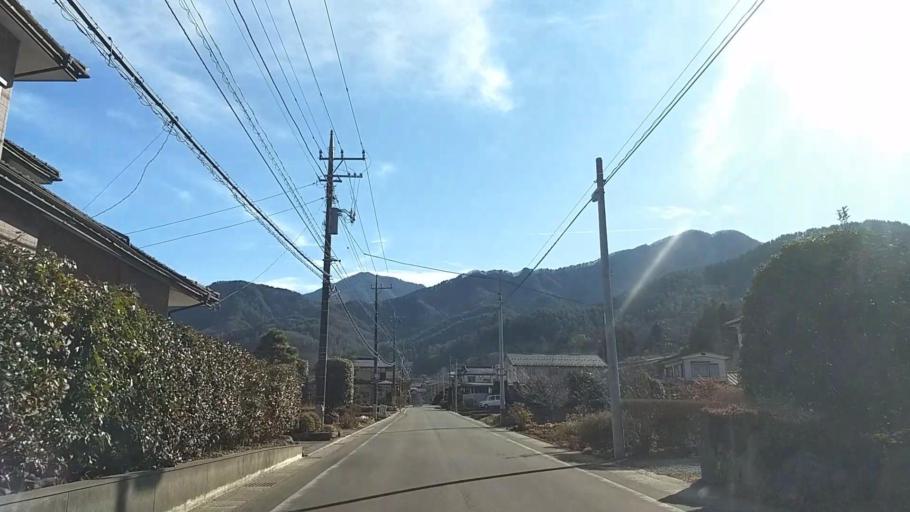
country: JP
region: Yamanashi
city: Otsuki
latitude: 35.5363
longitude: 138.9084
